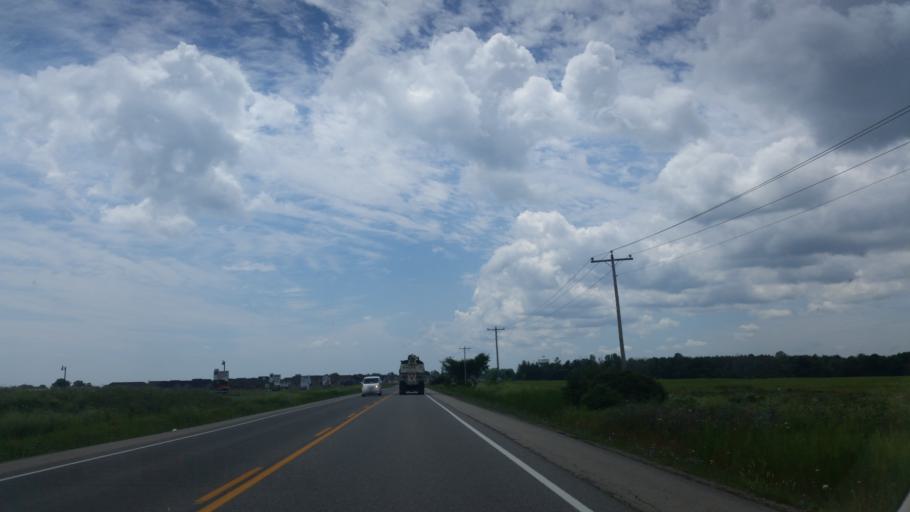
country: CA
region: Ontario
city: Norfolk County
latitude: 42.7985
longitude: -80.1712
